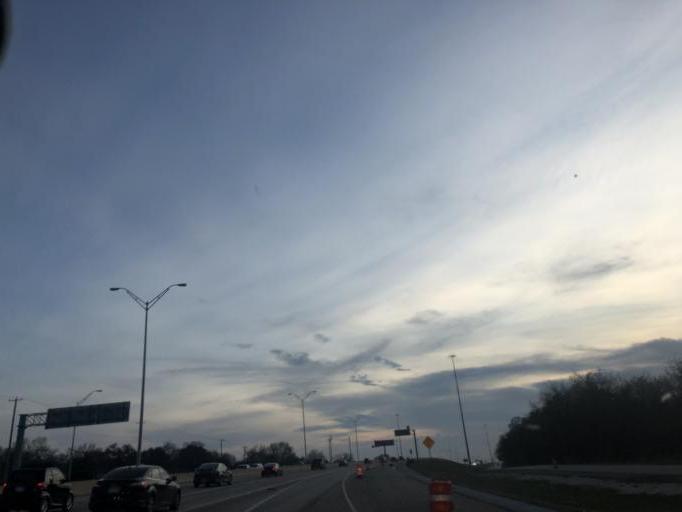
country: US
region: Texas
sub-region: Dallas County
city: Cockrell Hill
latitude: 32.6872
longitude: -96.8482
